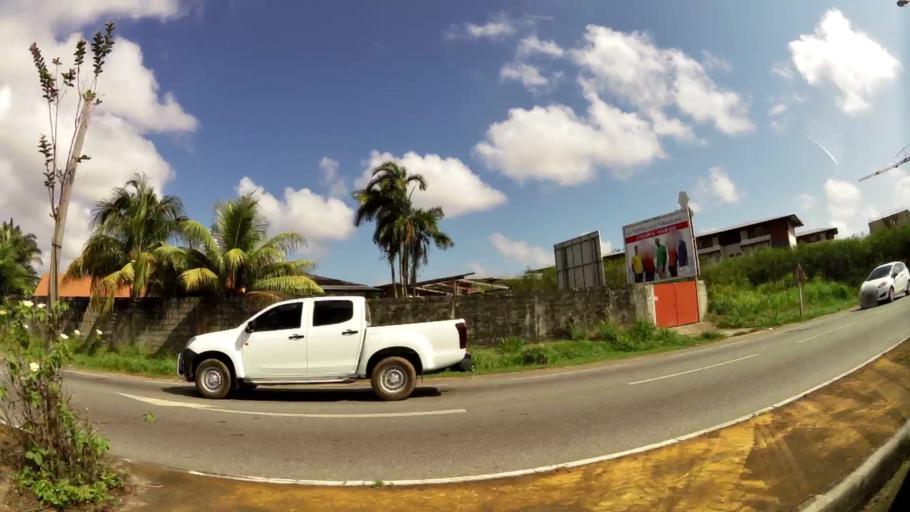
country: GF
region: Guyane
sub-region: Guyane
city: Cayenne
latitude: 4.9301
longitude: -52.3144
